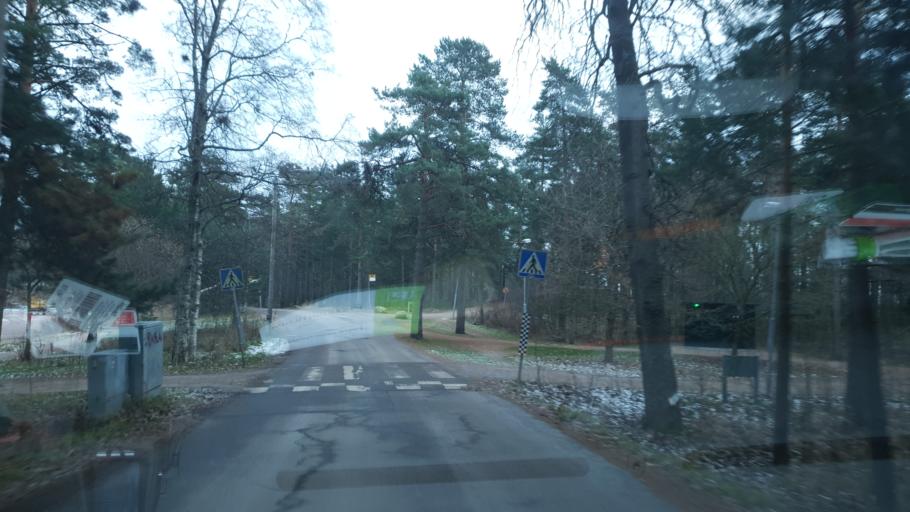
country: FI
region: Uusimaa
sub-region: Helsinki
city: Helsinki
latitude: 60.1805
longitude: 24.9891
